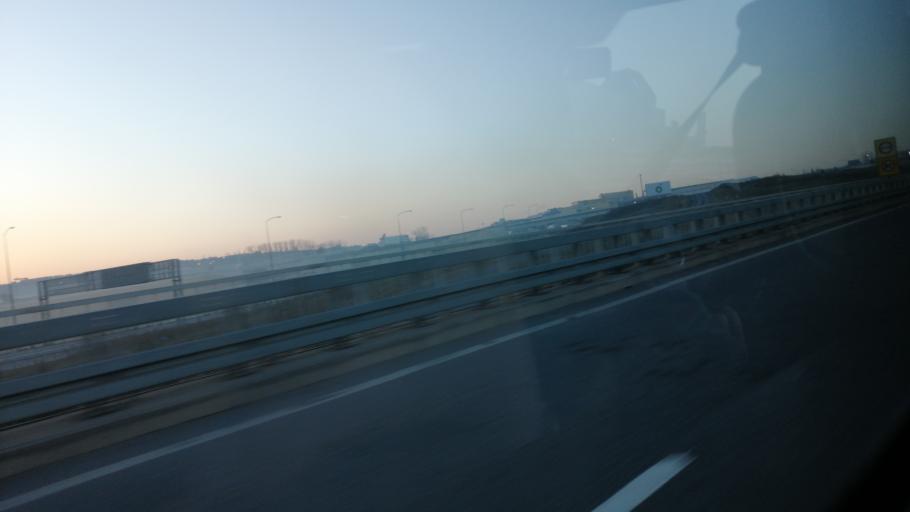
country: TR
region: Kocaeli
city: Tavsanli
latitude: 40.7968
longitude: 29.5102
